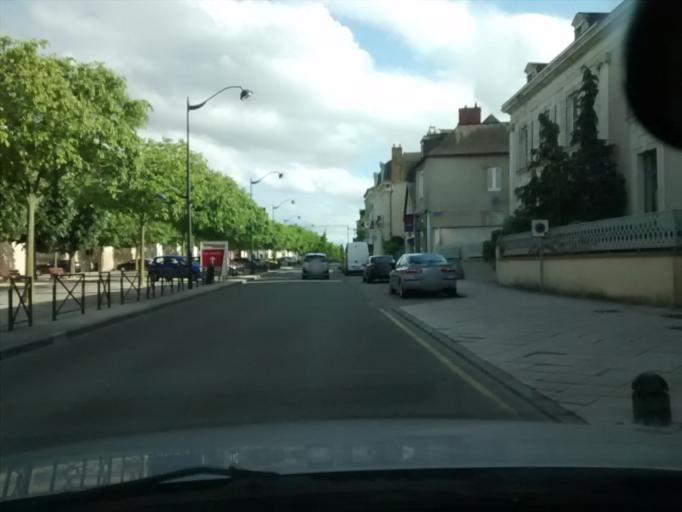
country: FR
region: Pays de la Loire
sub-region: Departement de la Mayenne
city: Chateau-Gontier
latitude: 47.8279
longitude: -0.7082
